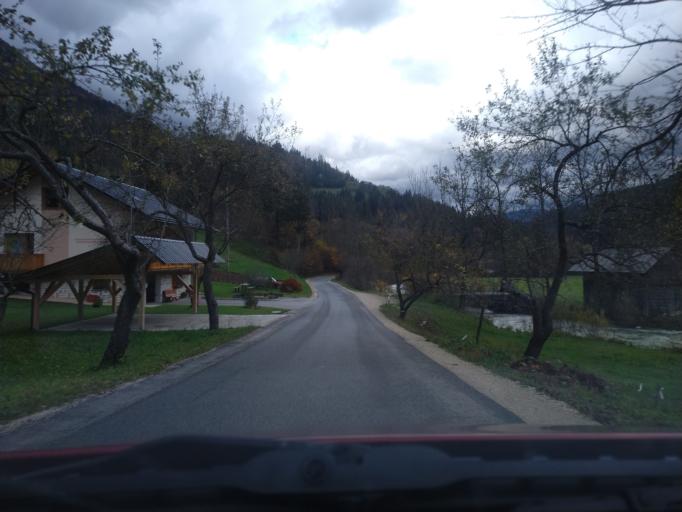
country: SI
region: Luce
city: Luce
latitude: 46.3269
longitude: 14.7177
